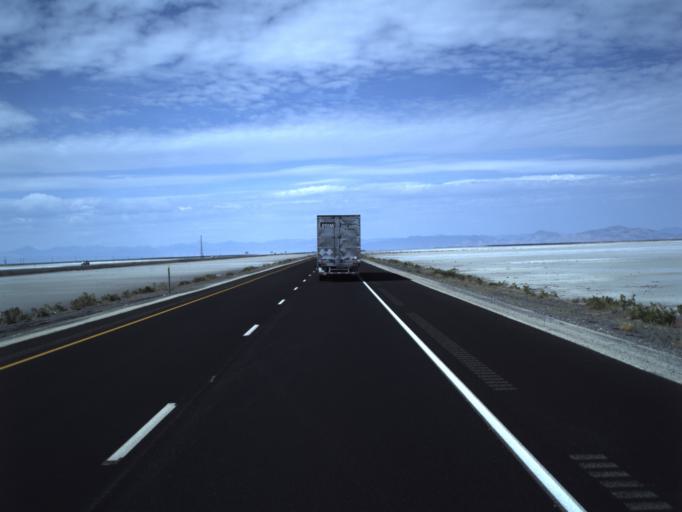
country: US
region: Utah
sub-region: Tooele County
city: Wendover
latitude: 40.7323
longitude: -113.5202
